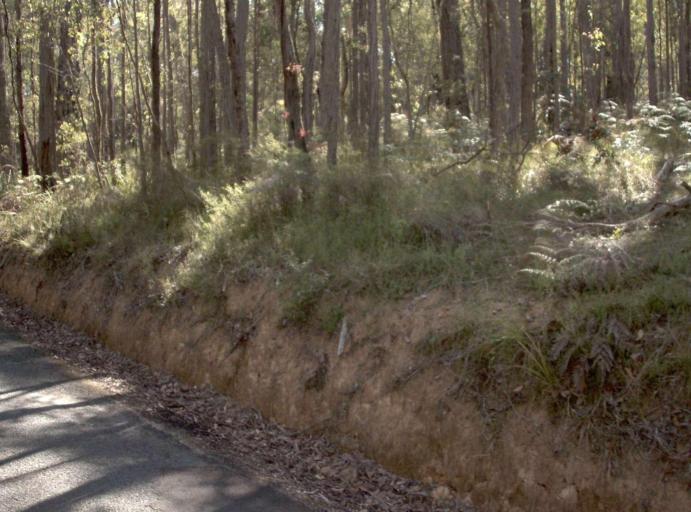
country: AU
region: New South Wales
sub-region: Bombala
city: Bombala
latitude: -37.3855
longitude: 148.6174
